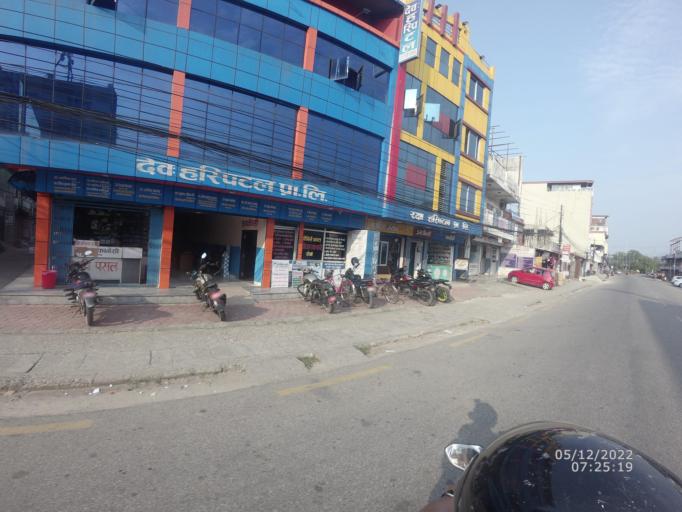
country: NP
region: Central Region
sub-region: Narayani Zone
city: Bharatpur
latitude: 27.6813
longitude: 84.4317
